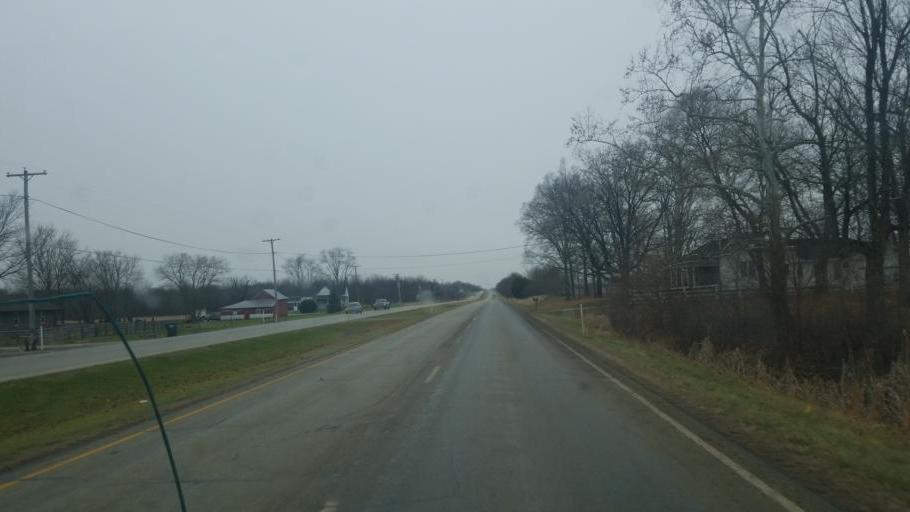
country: US
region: Indiana
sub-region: Hancock County
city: Greenfield
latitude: 39.7880
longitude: -85.7084
